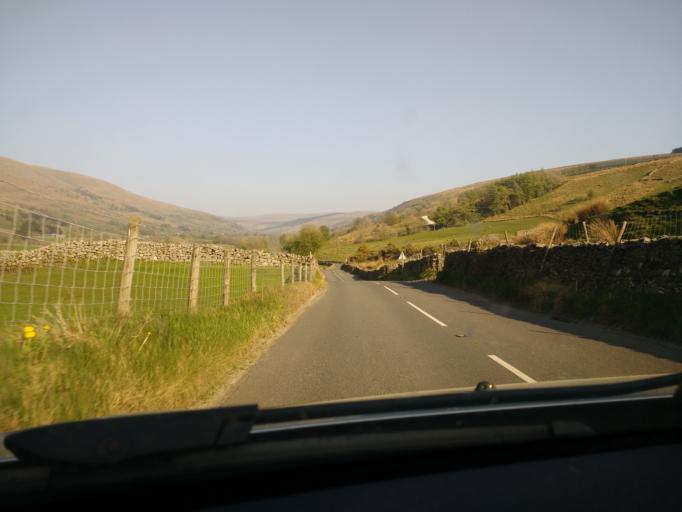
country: GB
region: England
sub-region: Cumbria
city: Sedbergh
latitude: 54.3145
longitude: -2.4660
